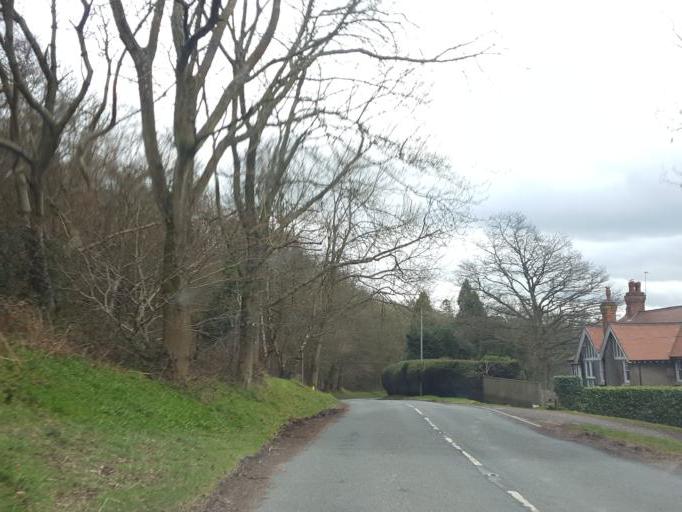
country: GB
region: England
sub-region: Worcestershire
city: Great Malvern
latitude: 52.0986
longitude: -2.3418
